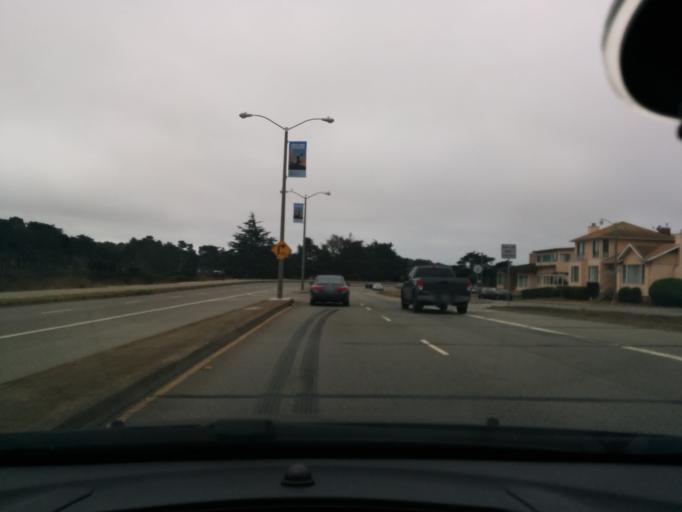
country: US
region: California
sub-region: San Mateo County
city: Daly City
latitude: 37.7300
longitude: -122.4900
